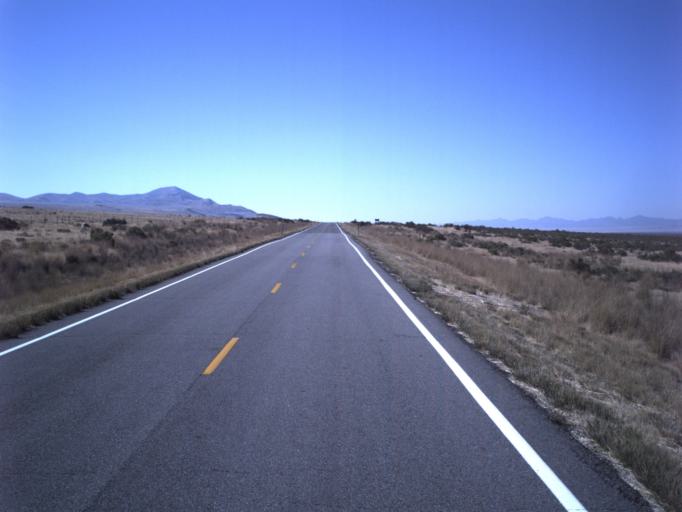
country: US
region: Utah
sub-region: Tooele County
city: Grantsville
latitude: 40.6478
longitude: -112.6859
